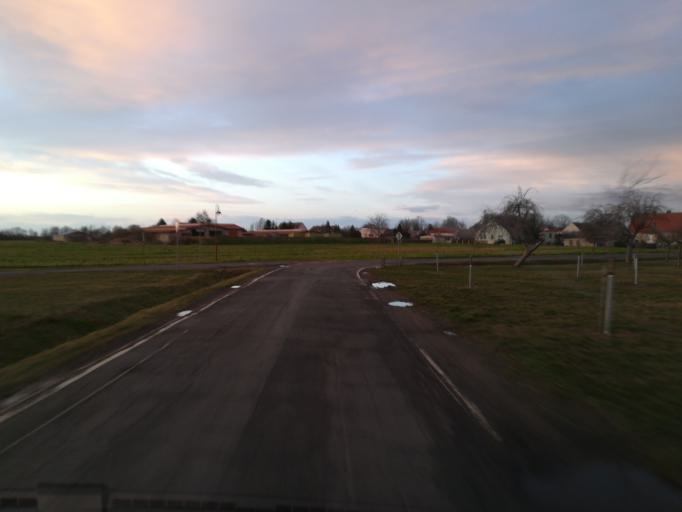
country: DE
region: Saxony-Anhalt
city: Brehna
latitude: 51.5239
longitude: 12.2287
